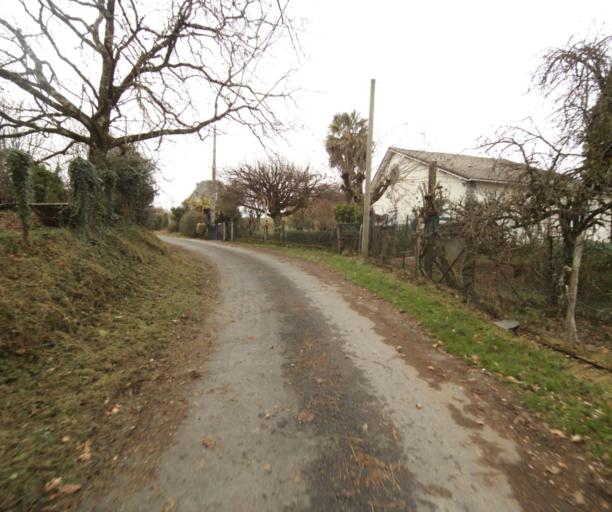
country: FR
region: Limousin
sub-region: Departement de la Correze
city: Saint-Mexant
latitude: 45.2537
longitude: 1.6618
